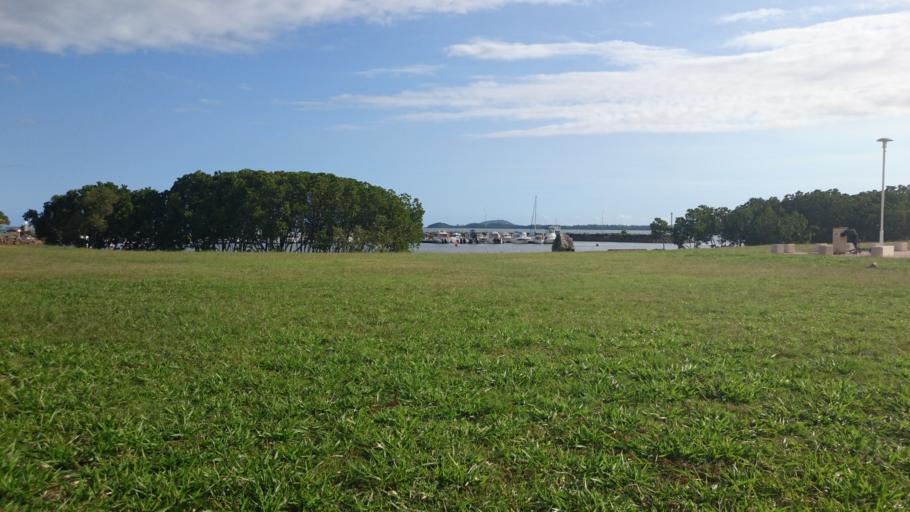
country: NC
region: South Province
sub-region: Le Mont-Dore
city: Mont-Dore
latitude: -22.2302
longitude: 166.5244
